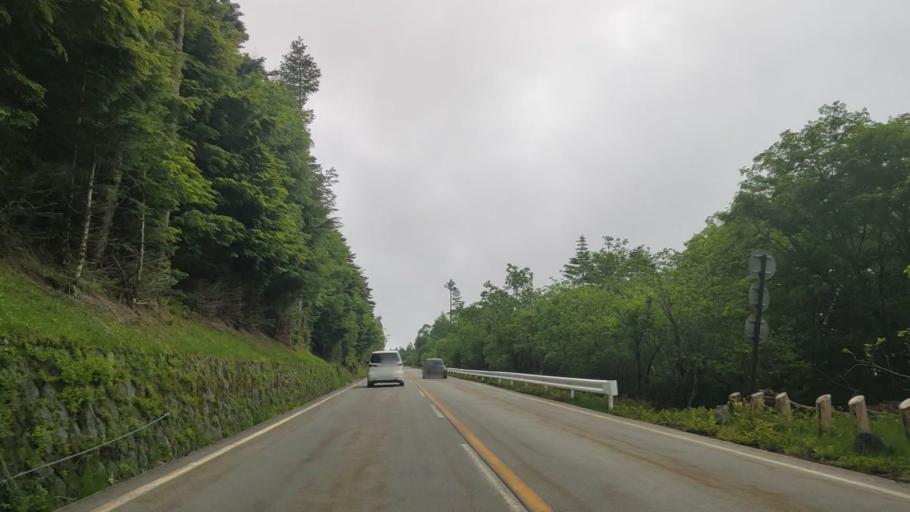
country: JP
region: Yamanashi
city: Fujikawaguchiko
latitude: 35.3943
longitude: 138.6917
